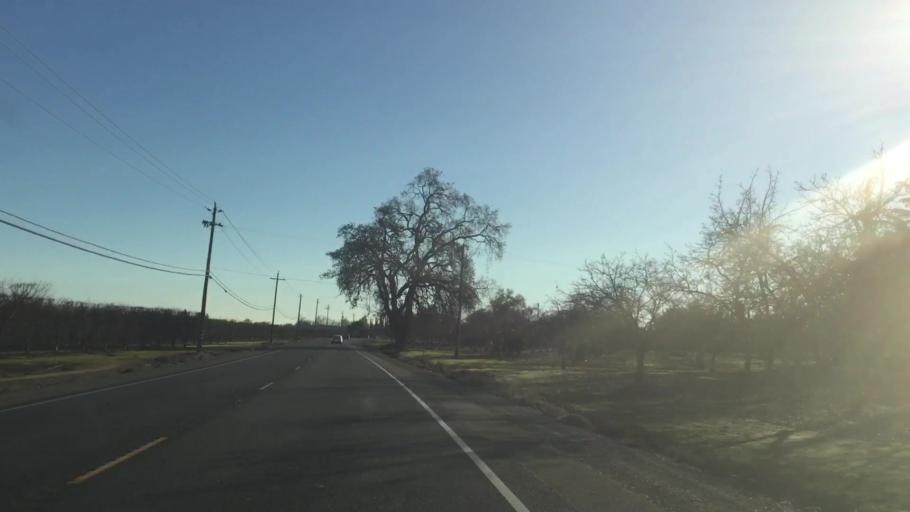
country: US
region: California
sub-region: Sutter County
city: Live Oak
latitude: 39.2908
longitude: -121.5949
